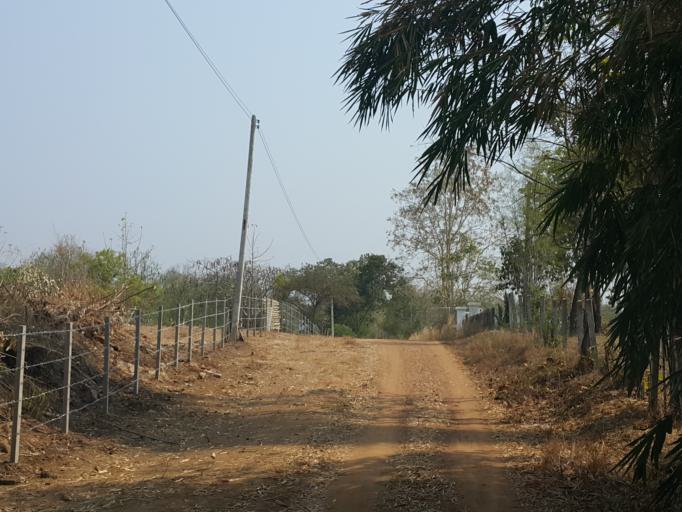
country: TH
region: Chiang Mai
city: Mae On
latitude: 18.7603
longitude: 99.2346
